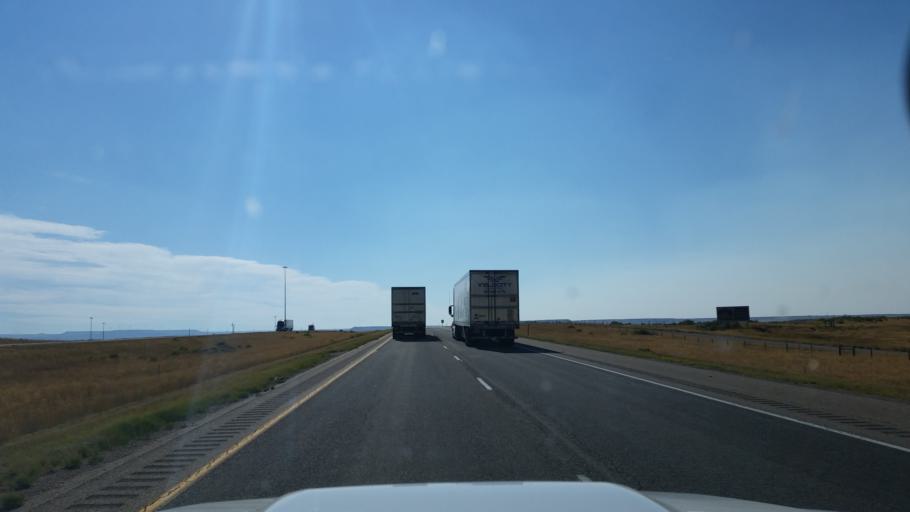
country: US
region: Wyoming
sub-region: Uinta County
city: Lyman
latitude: 41.3687
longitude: -110.2896
